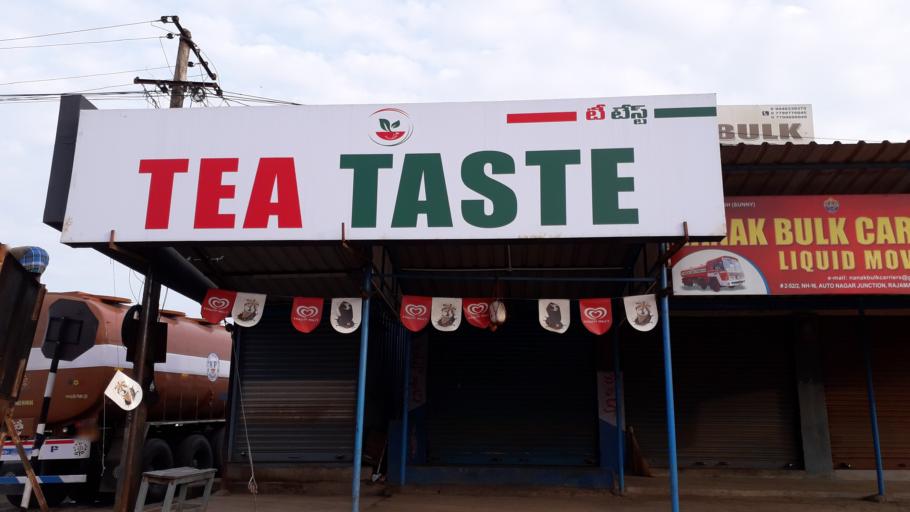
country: IN
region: Andhra Pradesh
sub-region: East Godavari
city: Rajahmundry
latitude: 17.0353
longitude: 81.8284
